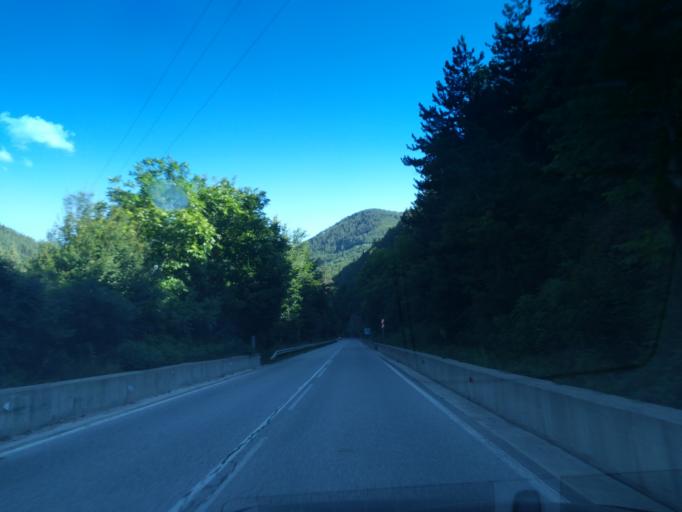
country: BG
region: Smolyan
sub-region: Obshtina Chepelare
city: Chepelare
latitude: 41.8349
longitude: 24.6834
